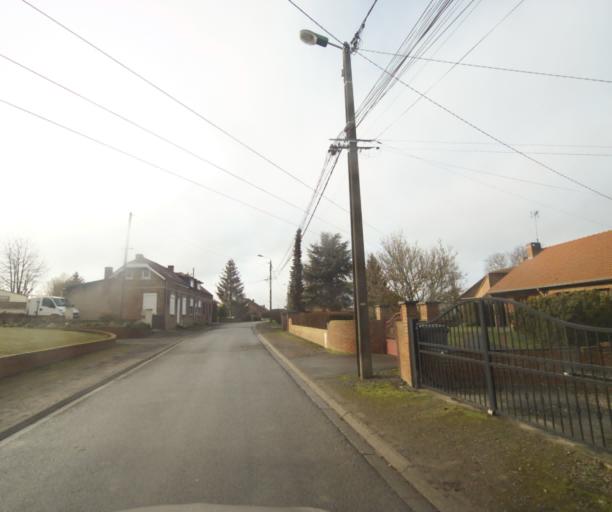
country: FR
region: Nord-Pas-de-Calais
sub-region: Departement du Nord
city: Maing
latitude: 50.3013
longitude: 3.4777
